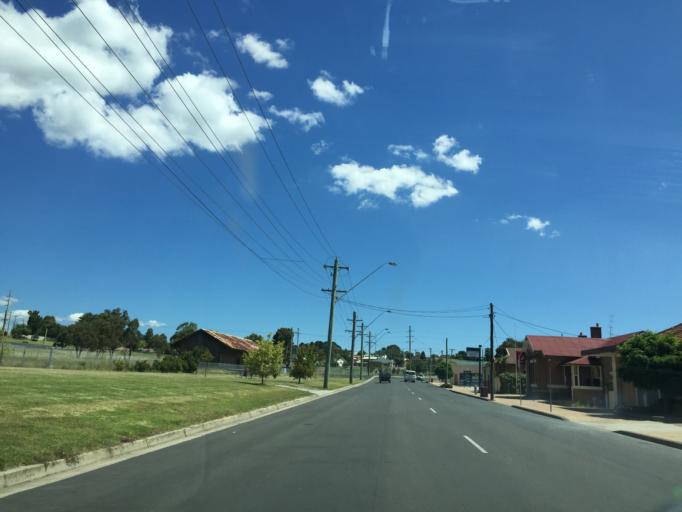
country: AU
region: New South Wales
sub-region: Lithgow
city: Portland
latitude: -33.4090
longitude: 150.0665
